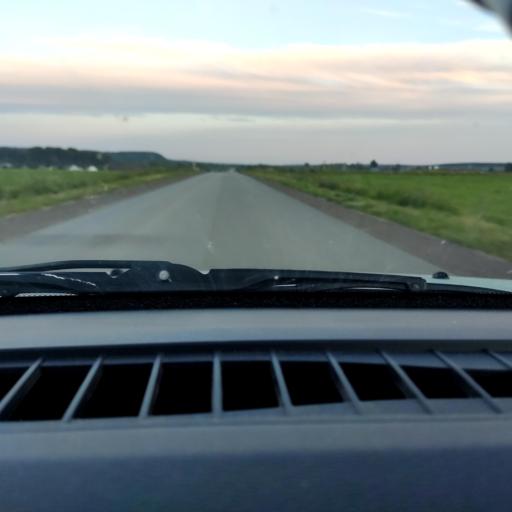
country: RU
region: Perm
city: Orda
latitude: 57.2217
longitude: 56.5740
